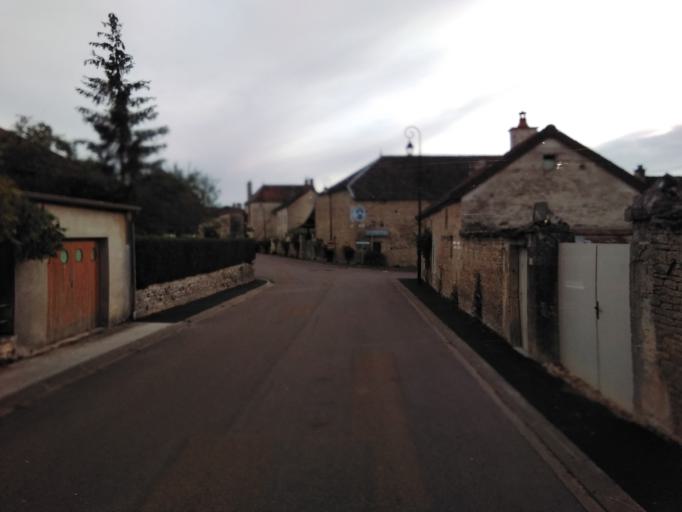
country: FR
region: Champagne-Ardenne
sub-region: Departement de l'Aube
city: Les Riceys
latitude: 47.9382
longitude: 4.3535
